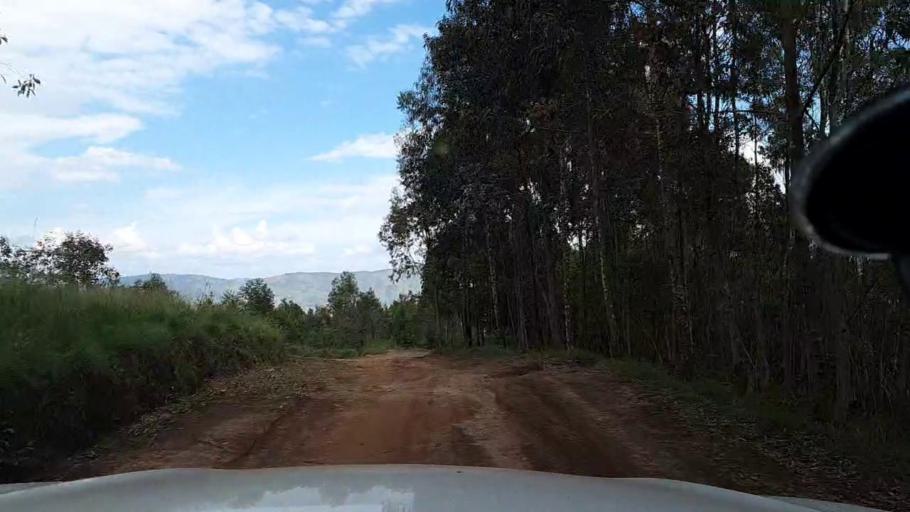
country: RW
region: Kigali
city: Kigali
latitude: -1.7823
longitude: 29.8356
